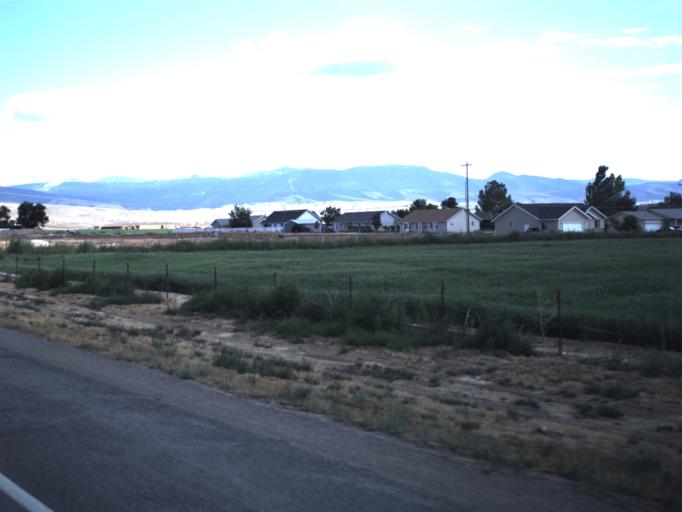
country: US
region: Utah
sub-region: Sanpete County
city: Gunnison
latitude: 39.1600
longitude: -111.8128
